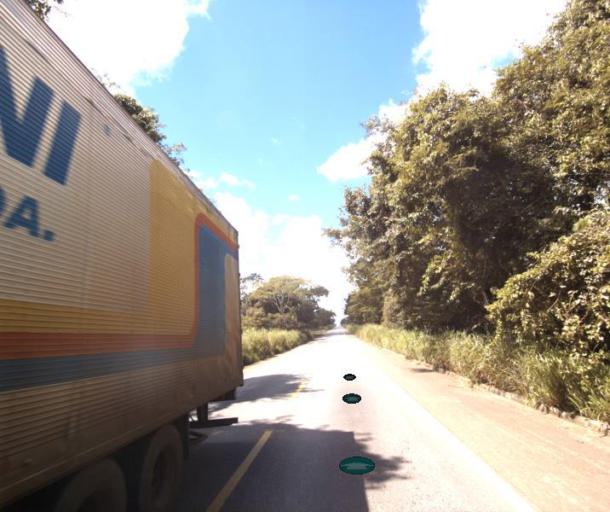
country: BR
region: Goias
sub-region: Petrolina De Goias
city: Petrolina de Goias
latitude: -15.9407
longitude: -49.1966
